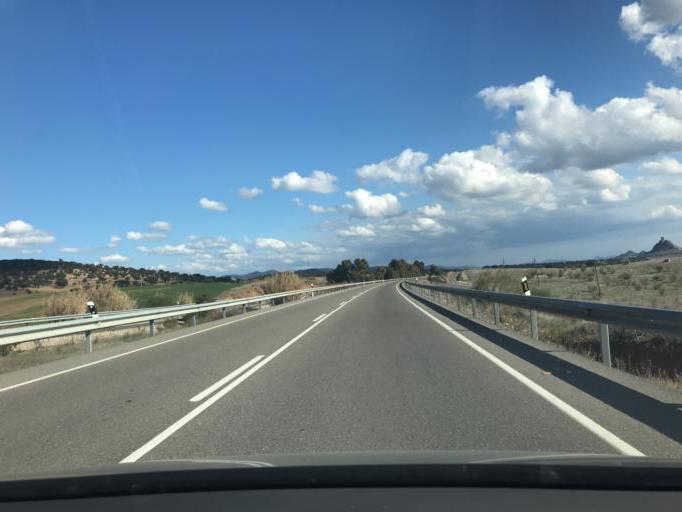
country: ES
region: Andalusia
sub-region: Province of Cordoba
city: Penarroya-Pueblonuevo
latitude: 38.2952
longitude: -5.2375
